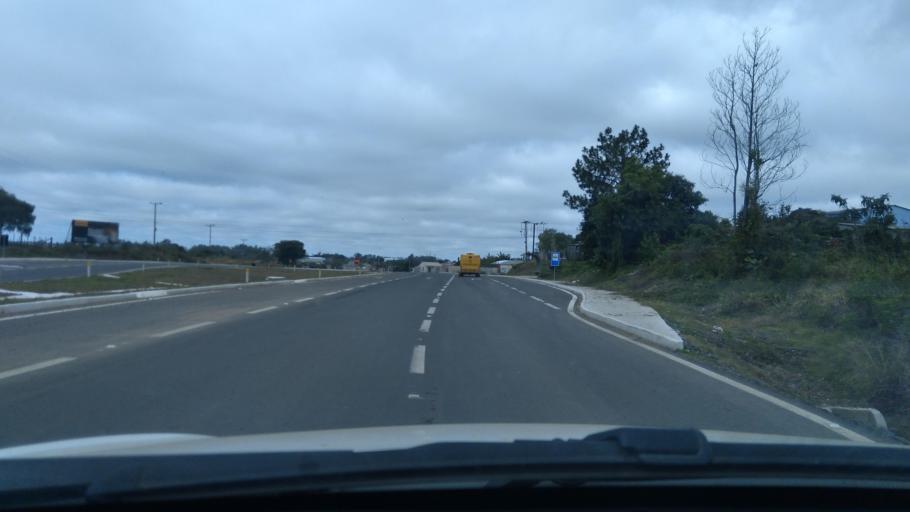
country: BR
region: Rio Grande do Sul
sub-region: Dom Pedrito
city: Dom Pedrito
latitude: -30.9631
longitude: -54.6727
